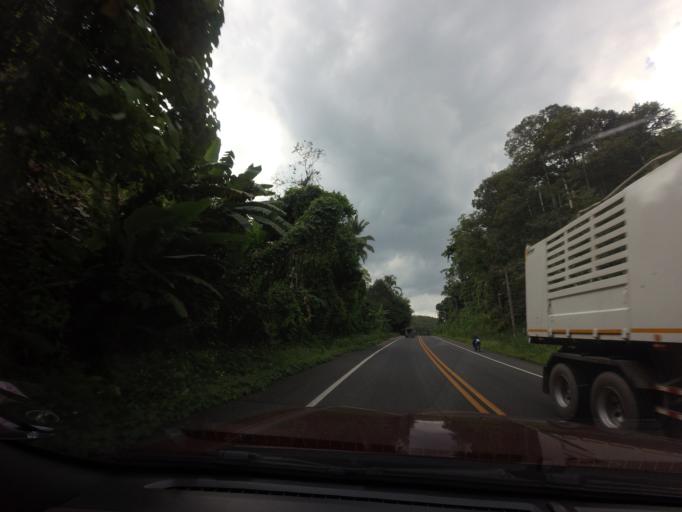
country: TH
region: Yala
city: Than To
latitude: 6.2056
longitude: 101.1693
